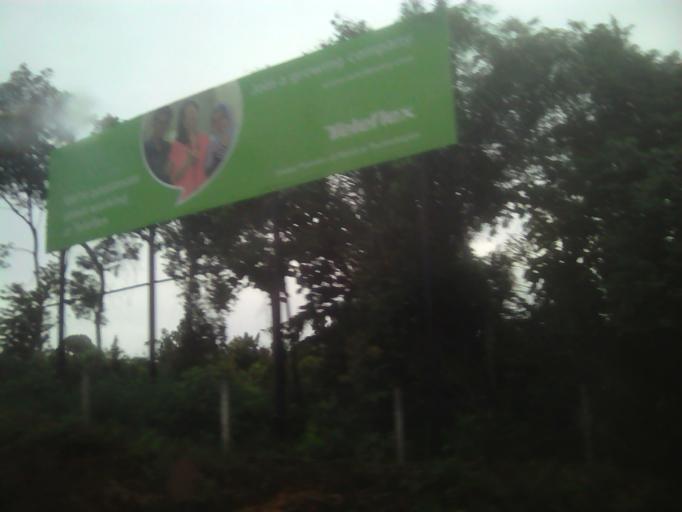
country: MY
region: Kedah
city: Kulim
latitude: 5.4181
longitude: 100.5331
